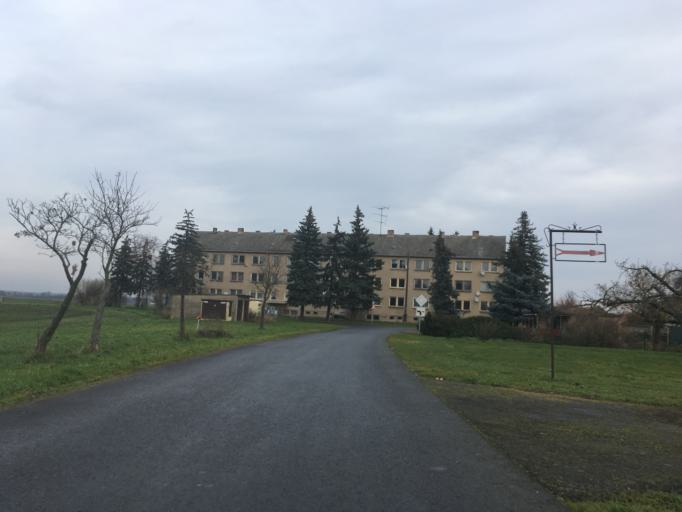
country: DE
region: Brandenburg
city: Letschin
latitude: 52.7048
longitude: 14.3501
